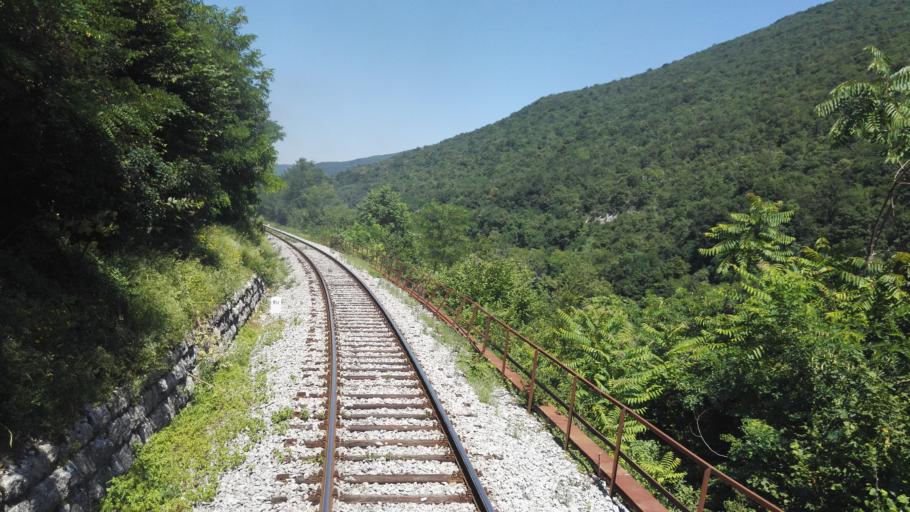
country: SI
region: Nova Gorica
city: Solkan
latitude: 45.9855
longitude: 13.6519
